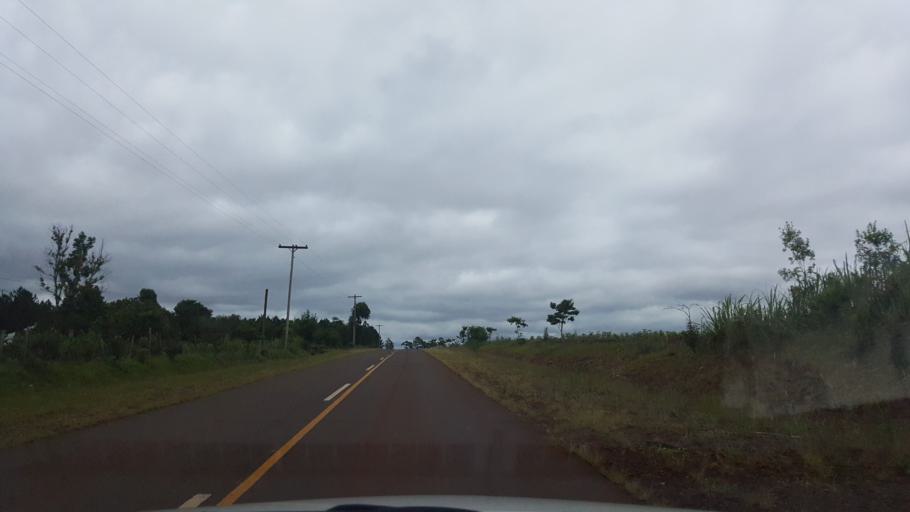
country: AR
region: Misiones
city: Ruiz de Montoya
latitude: -26.9686
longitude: -55.0754
